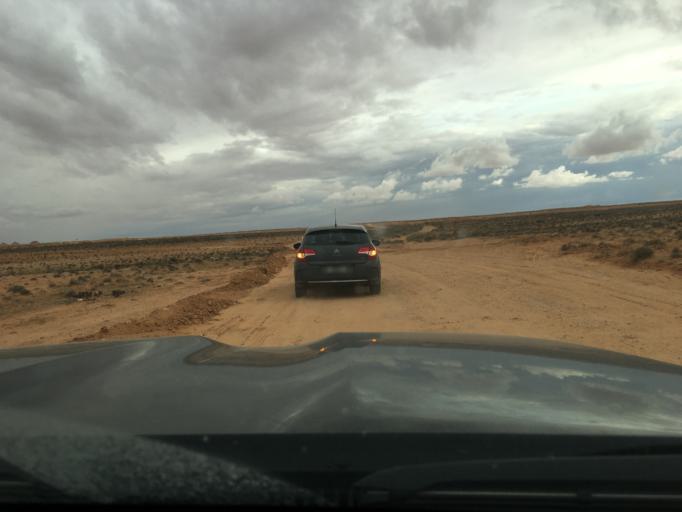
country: TN
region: Madanin
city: Medenine
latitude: 33.2622
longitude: 10.5720
